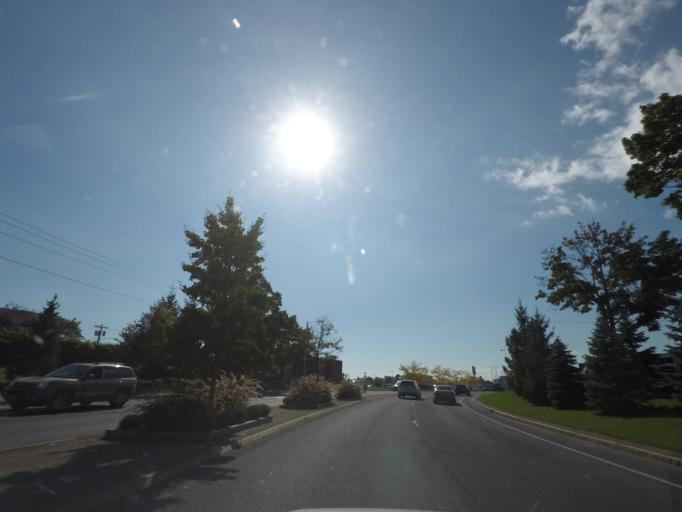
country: US
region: New York
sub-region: Albany County
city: West Albany
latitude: 42.6798
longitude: -73.7858
